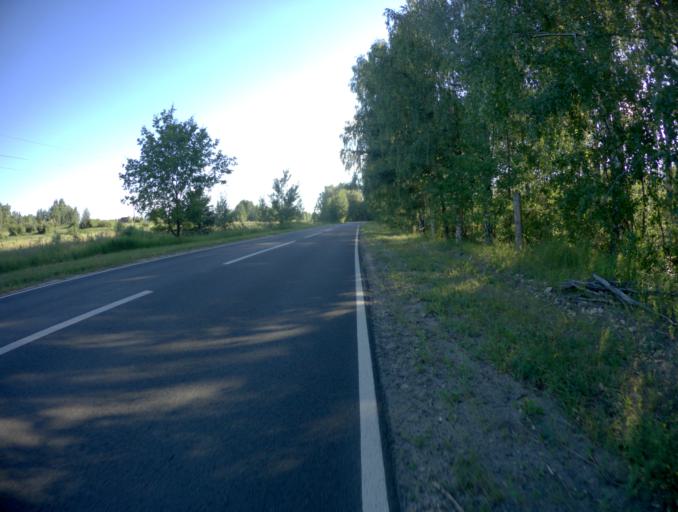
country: RU
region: Nizjnij Novgorod
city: Taremskoye
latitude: 56.0018
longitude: 42.9086
